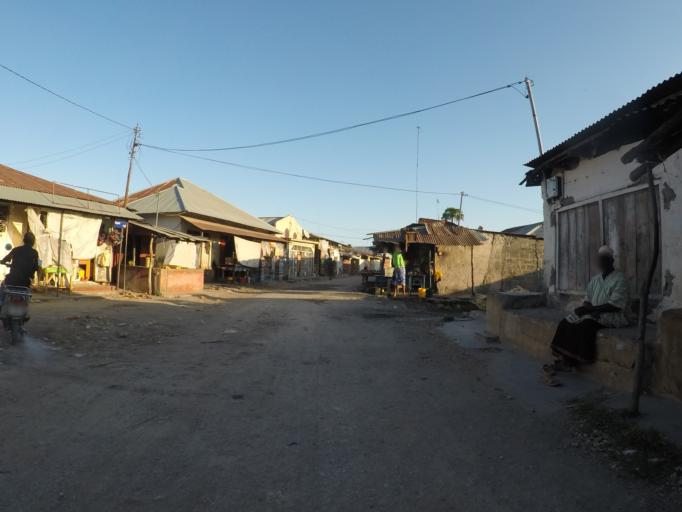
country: TZ
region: Zanzibar Urban/West
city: Zanzibar
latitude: -6.1604
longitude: 39.2179
